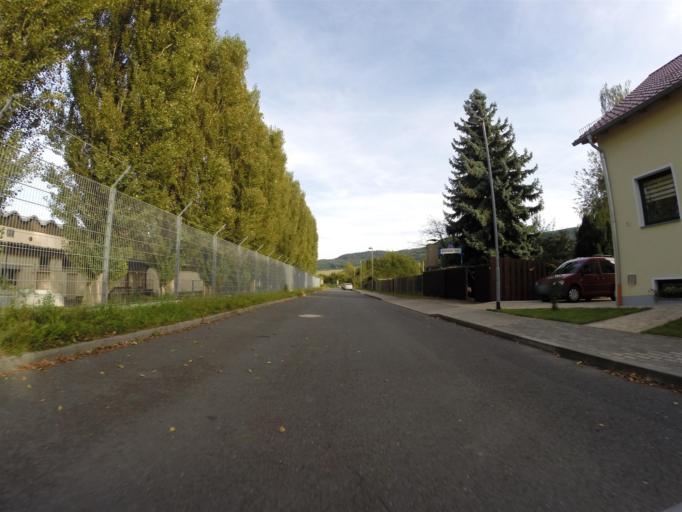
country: DE
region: Thuringia
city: Jena
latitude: 50.9531
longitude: 11.6168
